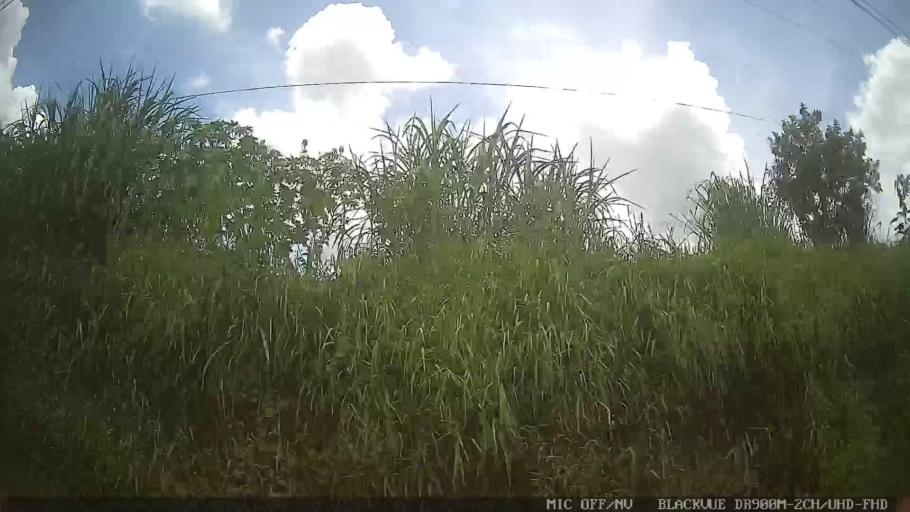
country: BR
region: Sao Paulo
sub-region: Atibaia
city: Atibaia
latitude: -23.0436
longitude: -46.5242
